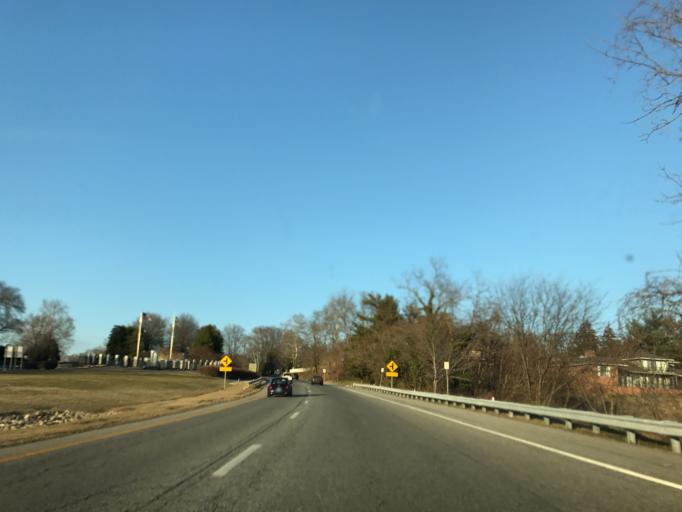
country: US
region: Maryland
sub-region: Anne Arundel County
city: Naval Academy
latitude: 38.9967
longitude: -76.4823
